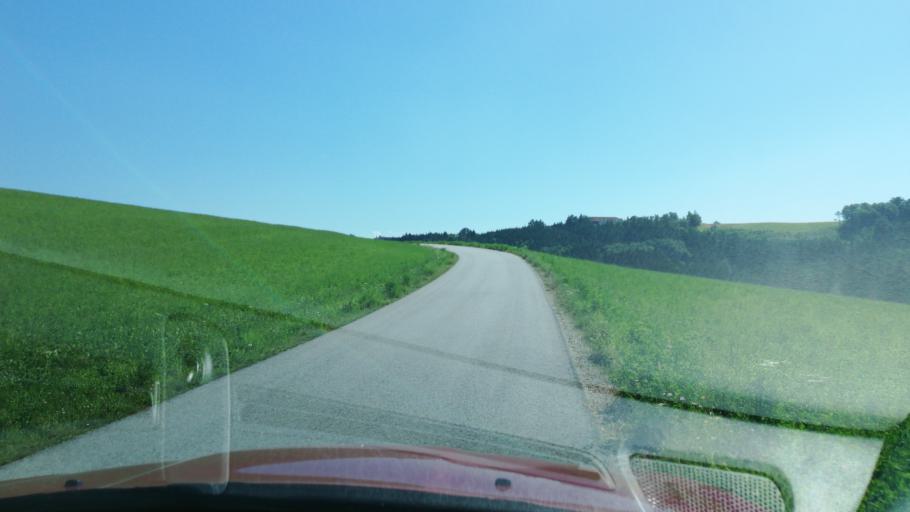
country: AT
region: Upper Austria
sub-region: Politischer Bezirk Rohrbach
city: Kleinzell im Muehlkreis
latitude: 48.4845
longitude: 14.0500
